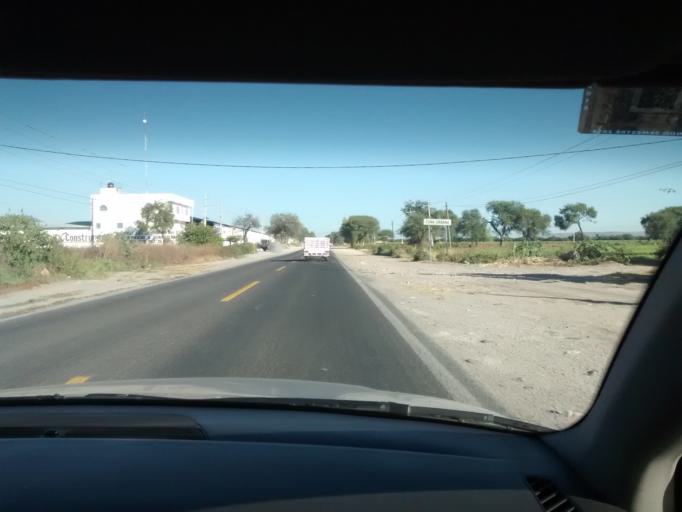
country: MX
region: Puebla
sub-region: Santiago Miahuatlan
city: San Jose Monte Chiquito
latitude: 18.5014
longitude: -97.4778
